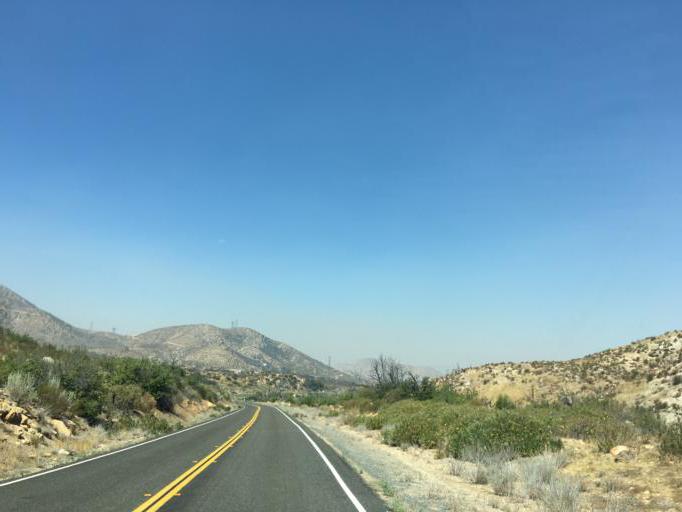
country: US
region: California
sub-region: Los Angeles County
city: Vincent
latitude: 34.4291
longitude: -118.1144
